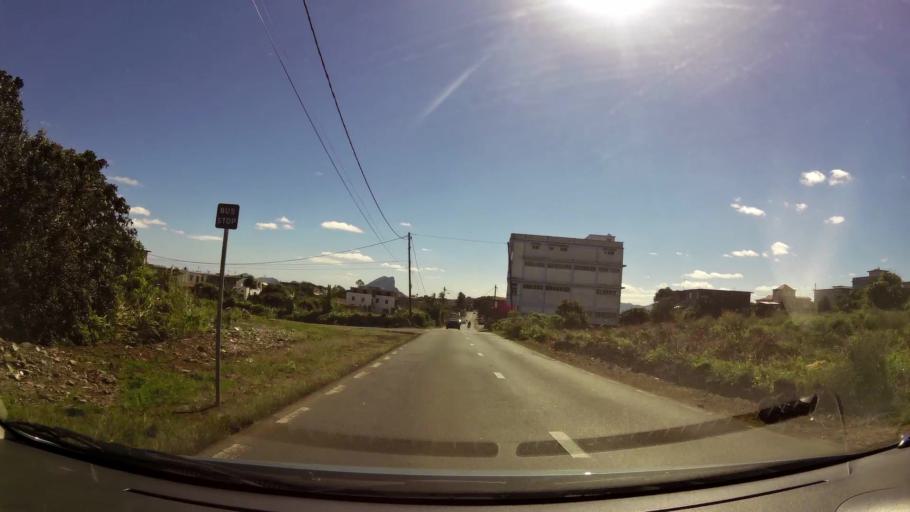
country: MU
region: Plaines Wilhems
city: Vacoas
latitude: -20.3309
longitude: 57.4868
